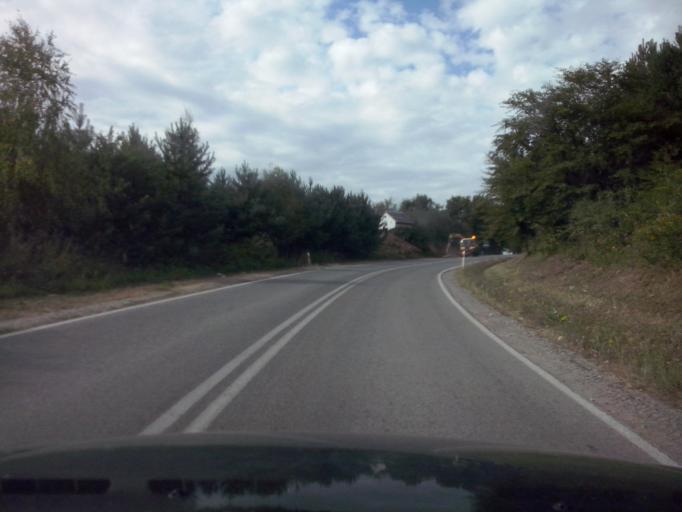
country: PL
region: Swietokrzyskie
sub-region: Powiat kielecki
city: Lagow
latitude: 50.7825
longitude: 21.0827
